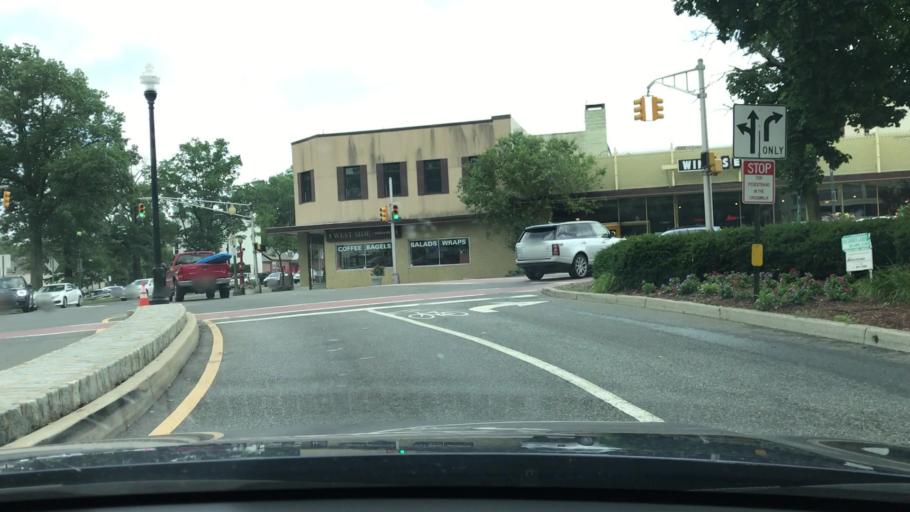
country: US
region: New Jersey
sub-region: Bergen County
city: Ridgewood
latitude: 40.9805
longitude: -74.1216
